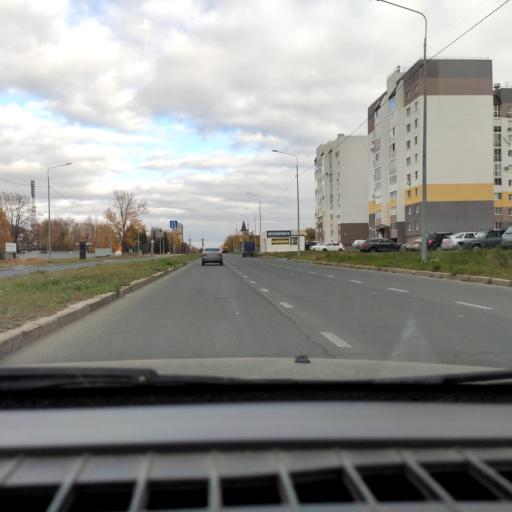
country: RU
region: Samara
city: Tol'yatti
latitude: 53.5009
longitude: 49.2693
